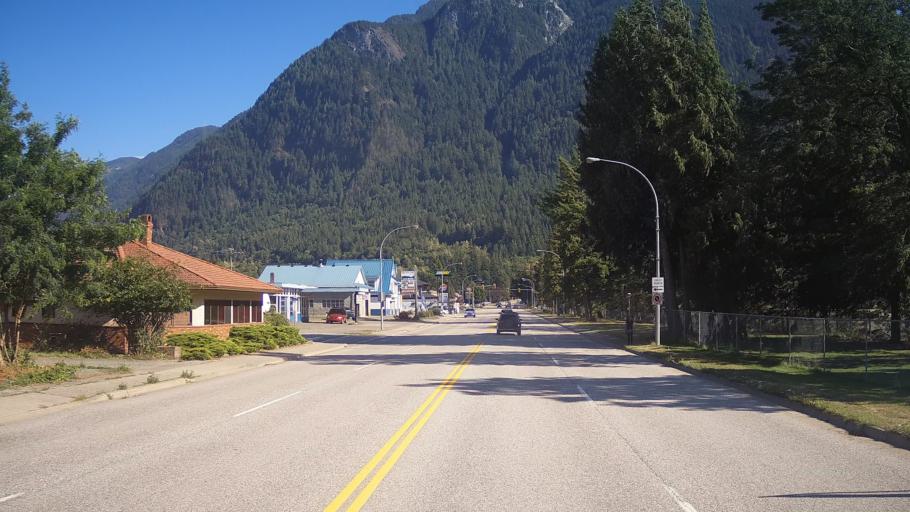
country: CA
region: British Columbia
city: Hope
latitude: 49.3805
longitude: -121.4460
